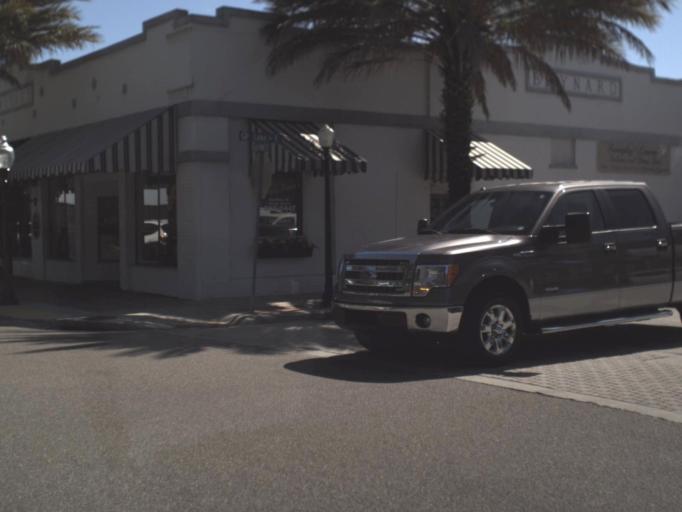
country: US
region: Florida
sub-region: Polk County
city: Auburndale
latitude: 28.0658
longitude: -81.7882
